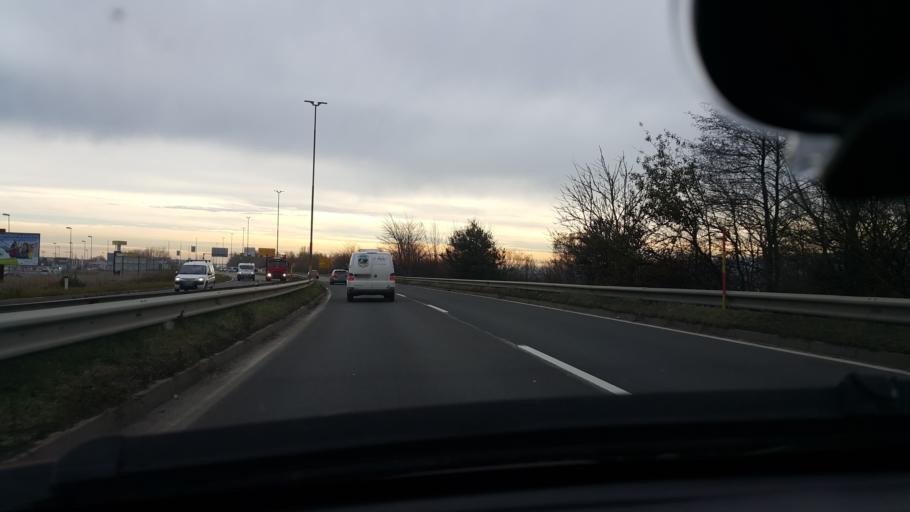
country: SI
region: Maribor
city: Razvanje
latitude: 46.5227
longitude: 15.6478
